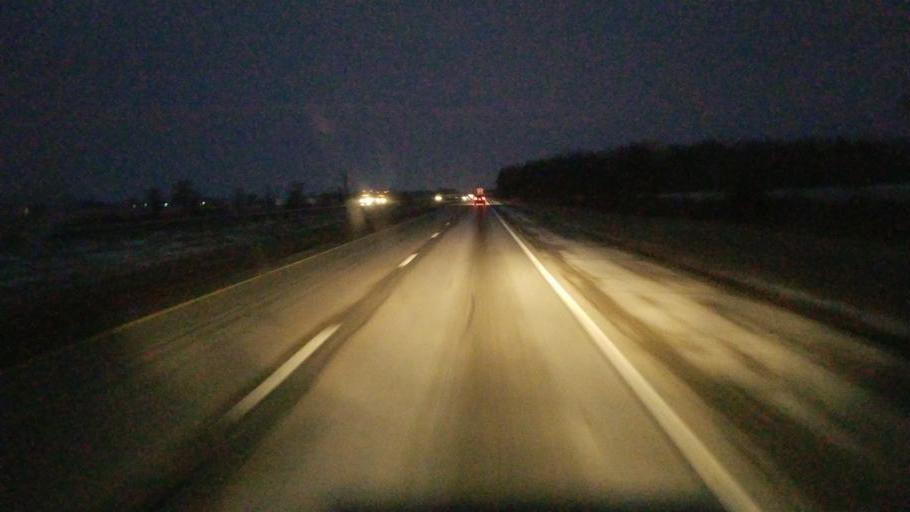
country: US
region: Ohio
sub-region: Preble County
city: Eaton
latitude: 39.8357
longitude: -84.6647
